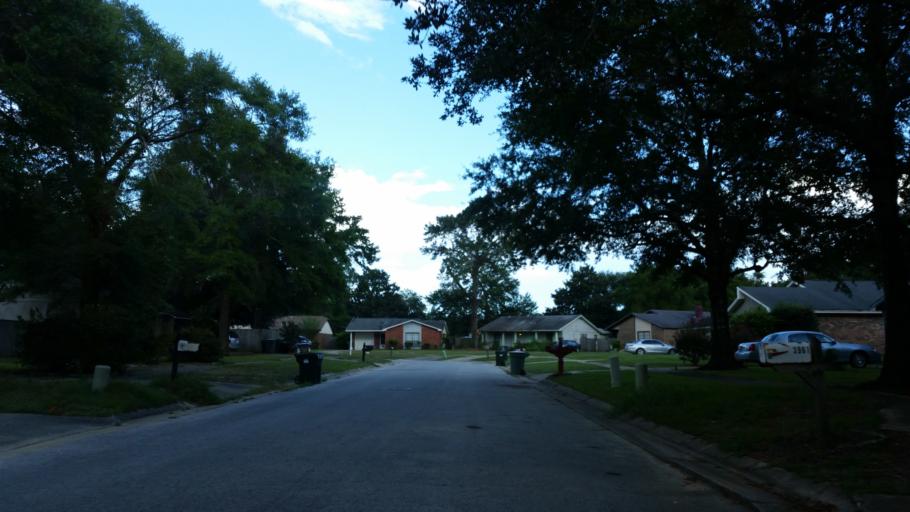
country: US
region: Florida
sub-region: Escambia County
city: Ferry Pass
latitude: 30.5005
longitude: -87.1707
